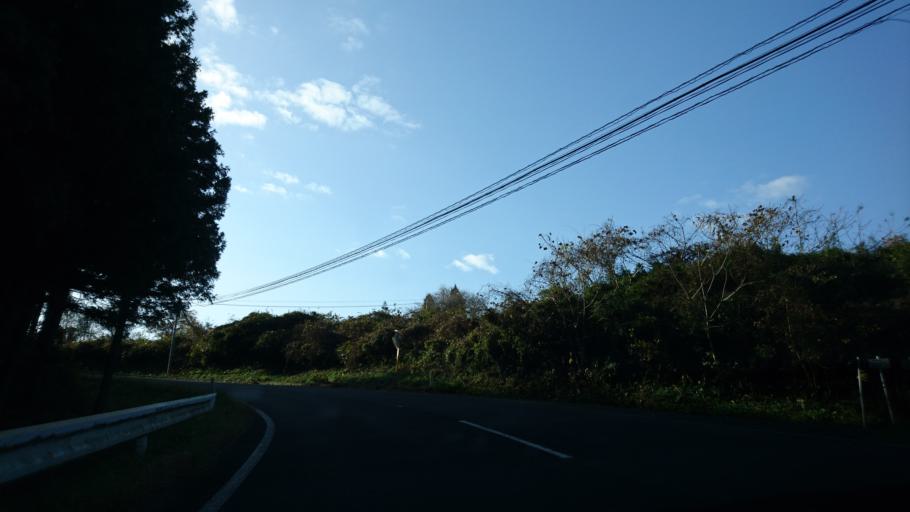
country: JP
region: Iwate
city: Ichinoseki
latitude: 38.8899
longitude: 141.2844
